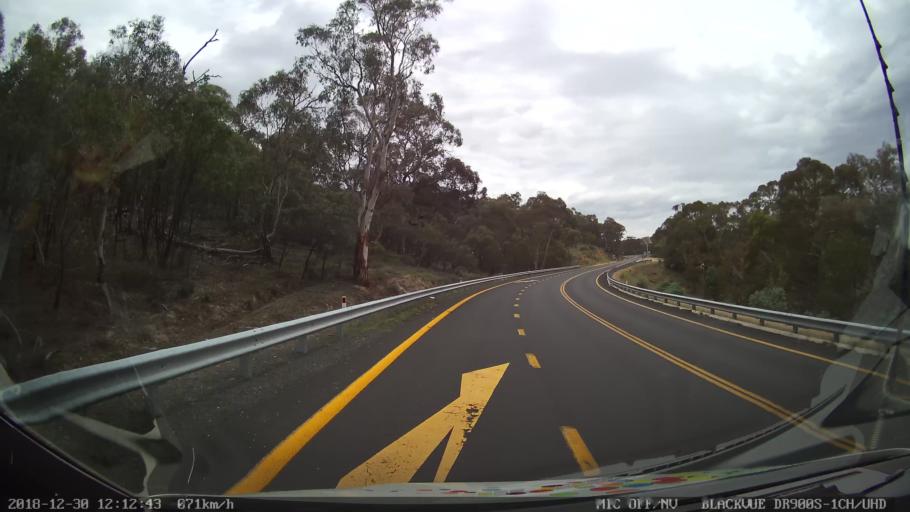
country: AU
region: New South Wales
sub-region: Snowy River
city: Jindabyne
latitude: -36.3552
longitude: 148.5872
